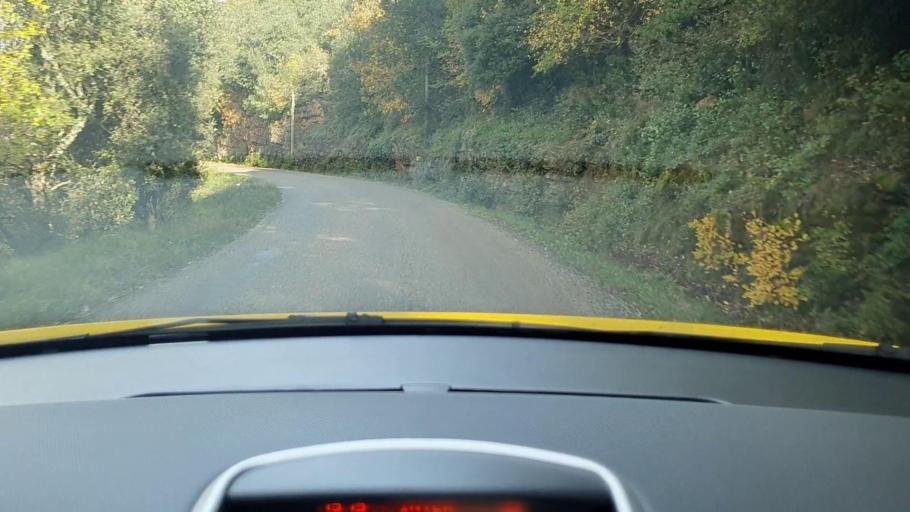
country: FR
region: Languedoc-Roussillon
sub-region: Departement du Gard
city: Anduze
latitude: 44.0517
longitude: 3.9219
